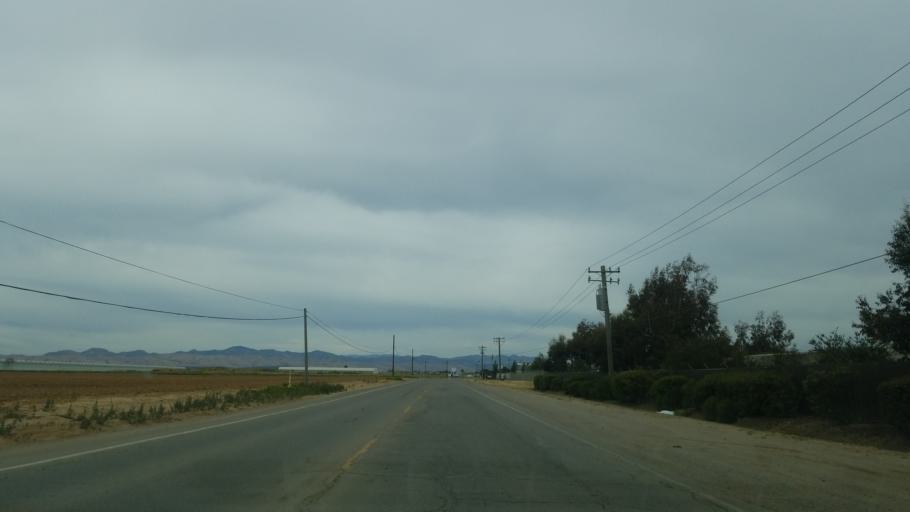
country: US
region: California
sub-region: Santa Barbara County
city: Santa Maria
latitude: 34.9212
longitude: -120.4817
